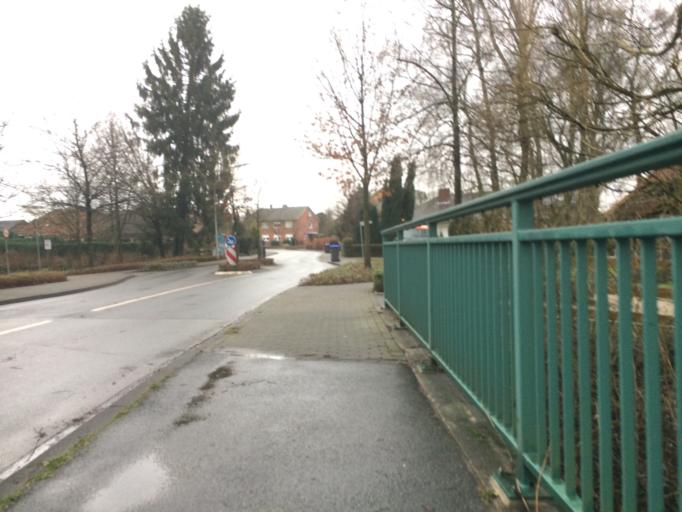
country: DE
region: North Rhine-Westphalia
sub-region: Regierungsbezirk Munster
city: Beelen
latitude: 51.9318
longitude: 8.1137
